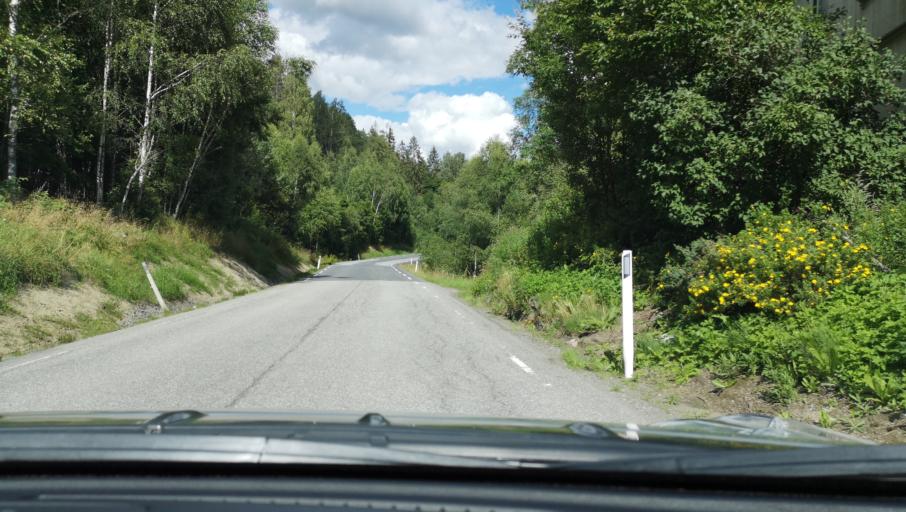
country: NO
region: Ostfold
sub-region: Hobol
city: Elvestad
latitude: 59.6392
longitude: 10.9664
